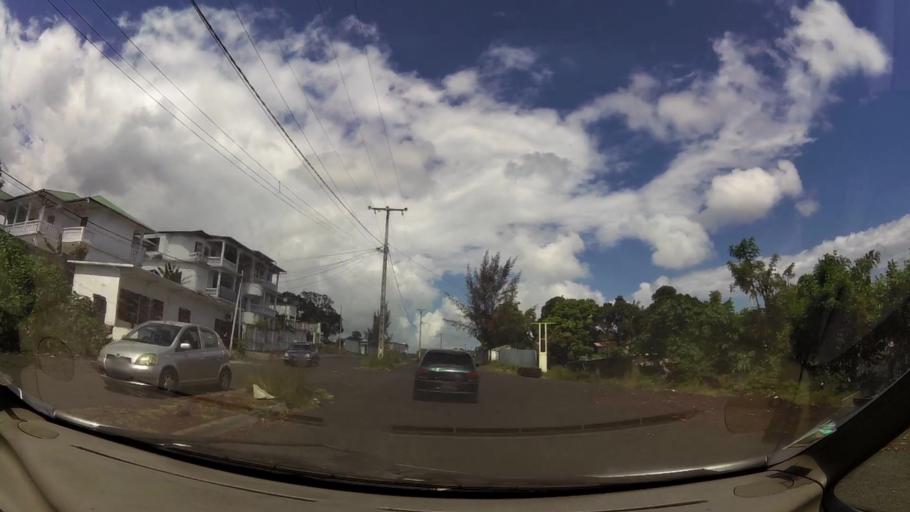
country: KM
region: Grande Comore
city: Mavingouni
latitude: -11.7224
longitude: 43.2451
